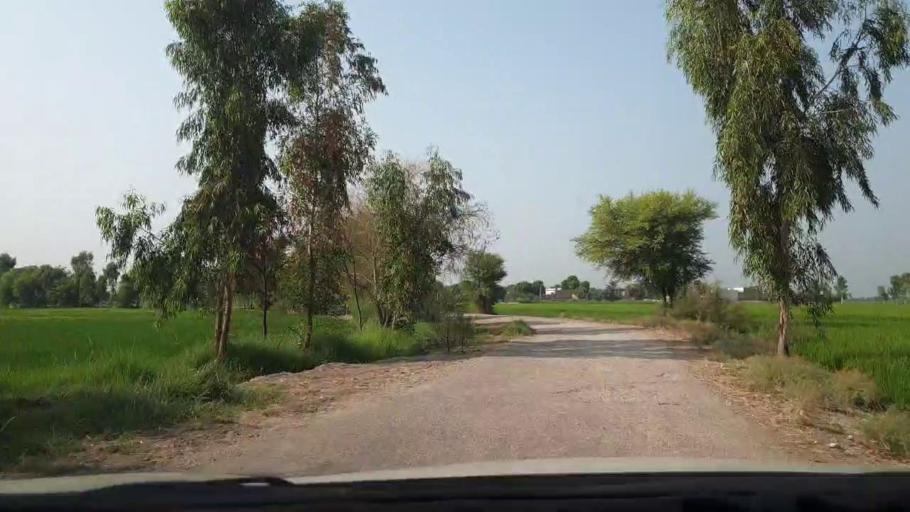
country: PK
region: Sindh
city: Goth Garelo
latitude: 27.4902
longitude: 68.1146
